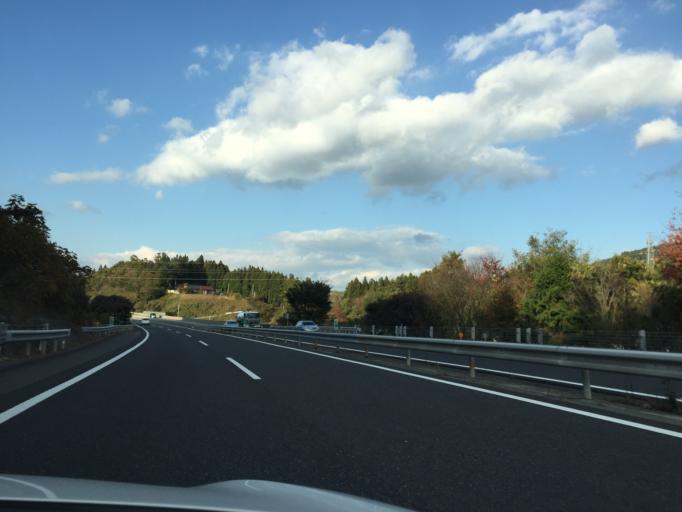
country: JP
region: Fukushima
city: Funehikimachi-funehiki
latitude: 37.2969
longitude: 140.6146
